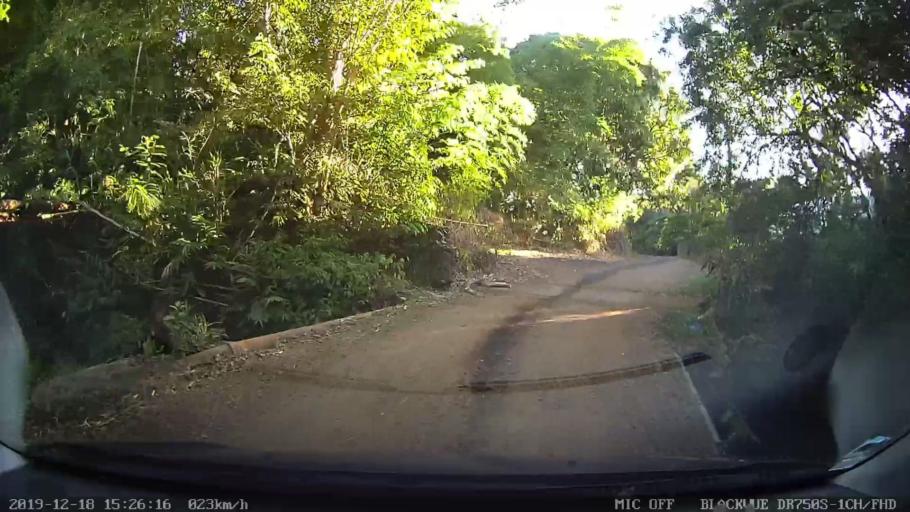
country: RE
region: Reunion
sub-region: Reunion
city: Bras-Panon
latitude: -21.0022
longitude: 55.6522
